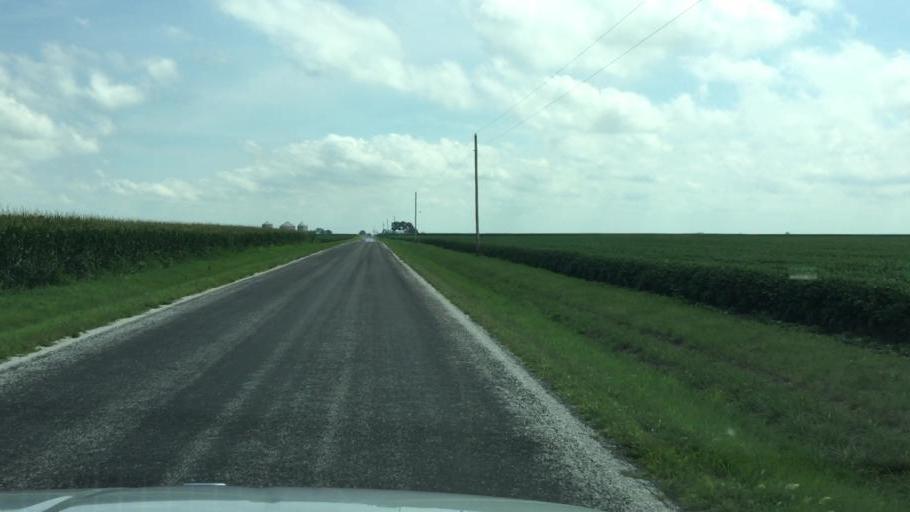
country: US
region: Illinois
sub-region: Hancock County
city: Carthage
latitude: 40.5333
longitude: -91.1769
